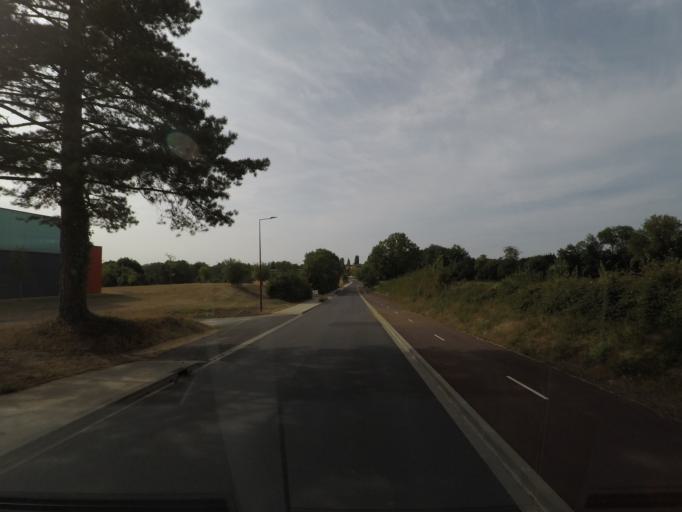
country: FR
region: Poitou-Charentes
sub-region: Departement des Deux-Sevres
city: Melle
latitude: 46.2284
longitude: -0.1287
